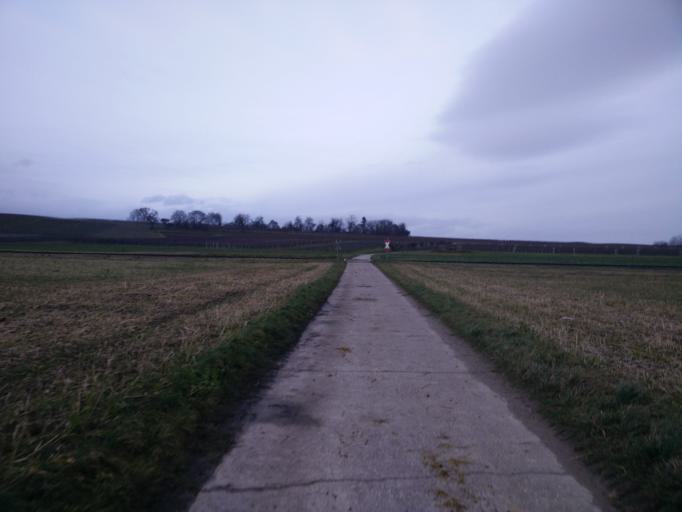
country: DE
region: Rheinland-Pfalz
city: Oberhausen
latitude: 49.1035
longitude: 8.0546
